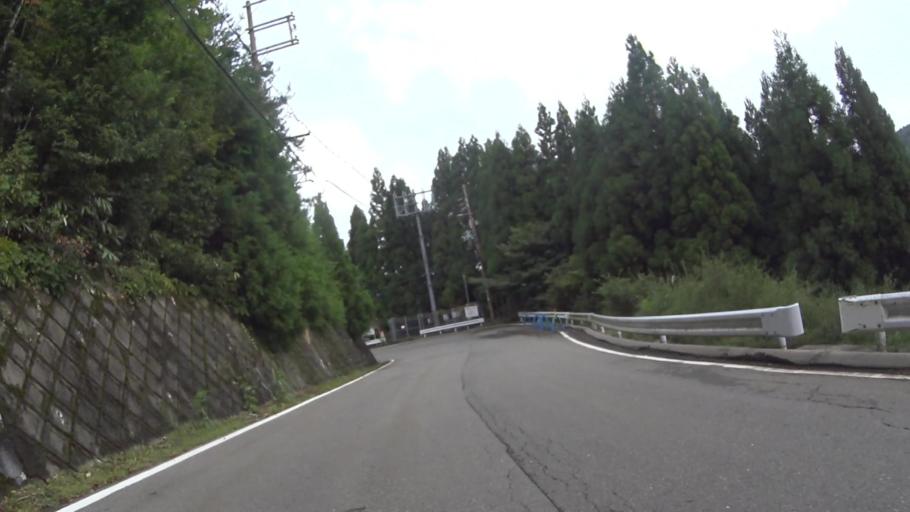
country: JP
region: Kyoto
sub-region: Kyoto-shi
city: Kamigyo-ku
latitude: 35.1600
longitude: 135.7797
